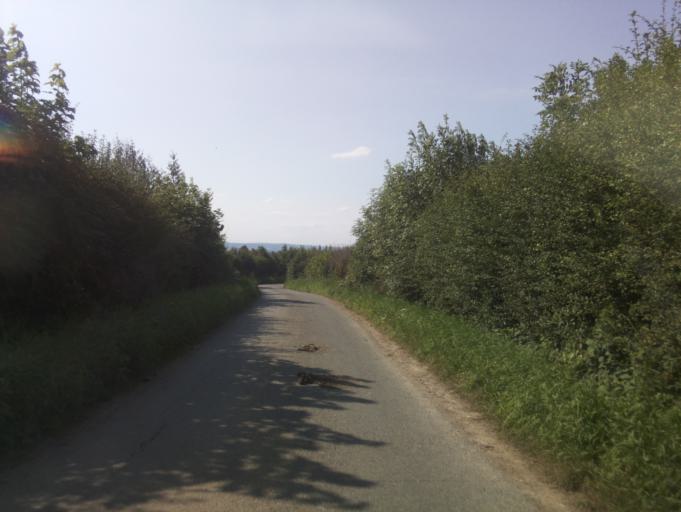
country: GB
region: England
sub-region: Gloucestershire
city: Dursley
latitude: 51.7062
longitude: -2.3151
